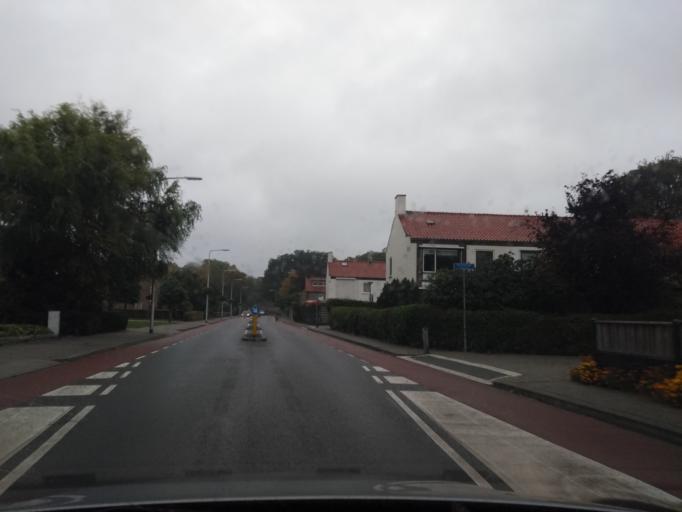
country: NL
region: Overijssel
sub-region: Gemeente Almelo
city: Almelo
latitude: 52.3536
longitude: 6.6724
